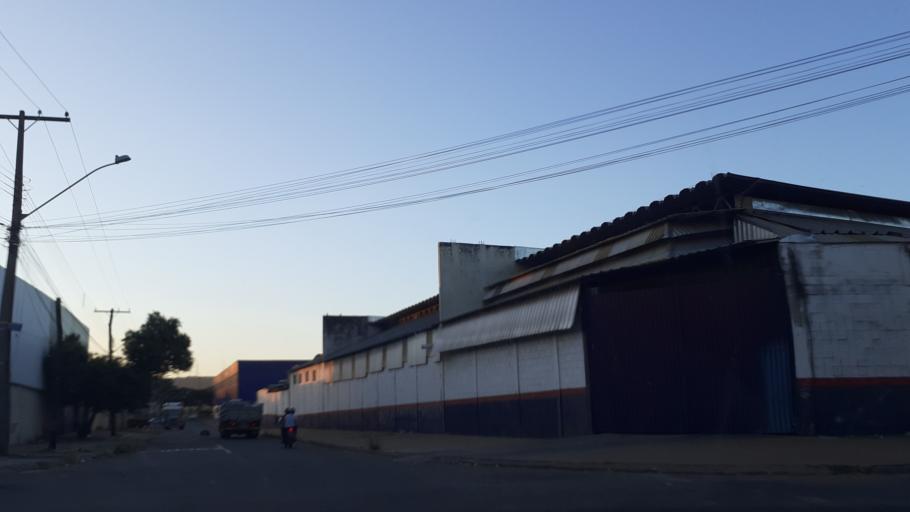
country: BR
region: Goias
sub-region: Goiania
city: Goiania
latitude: -16.7005
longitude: -49.3288
